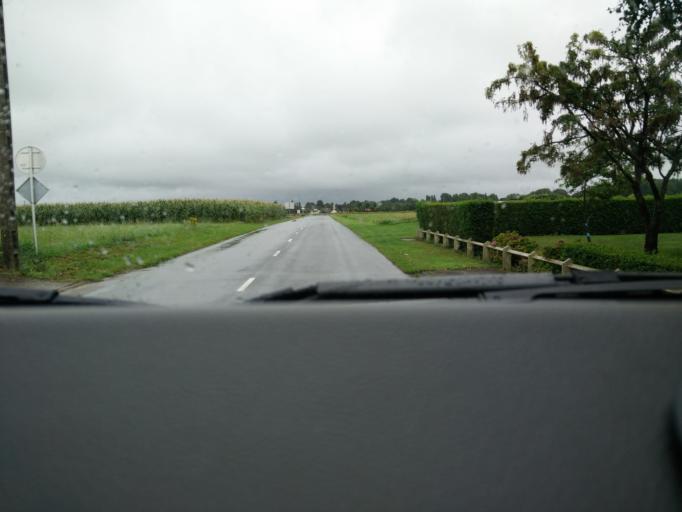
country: FR
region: Picardie
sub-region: Departement de la Somme
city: Rue
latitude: 50.2726
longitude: 1.6815
